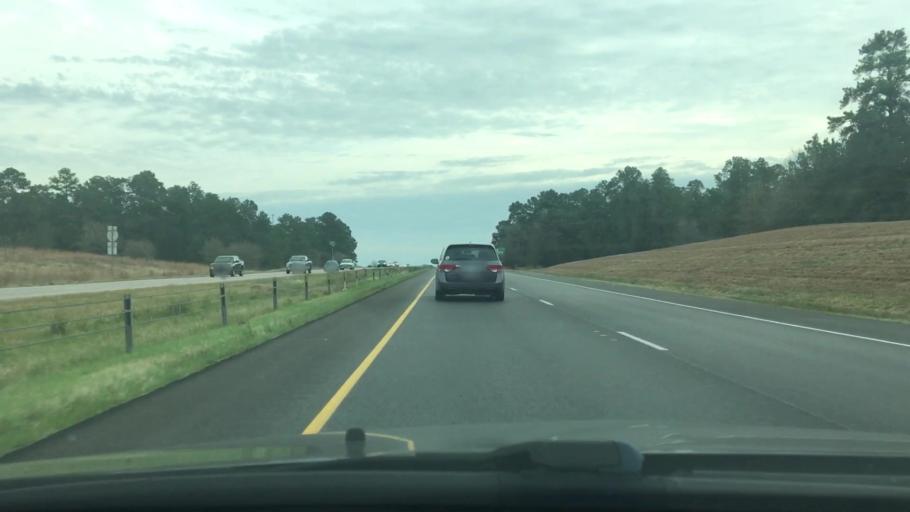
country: US
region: Texas
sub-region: Madison County
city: Madisonville
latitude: 30.8800
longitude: -95.7657
